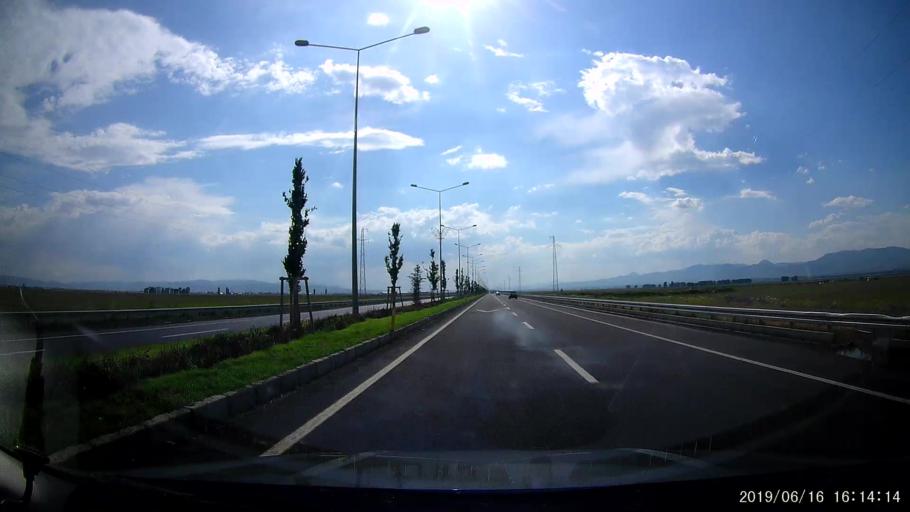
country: TR
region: Erzurum
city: Erzurum
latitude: 39.9604
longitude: 41.2545
